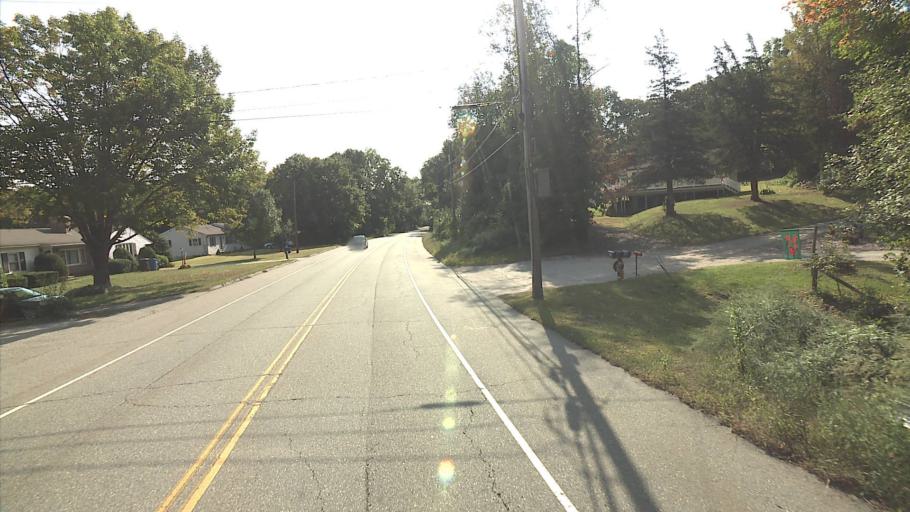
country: US
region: Connecticut
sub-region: New London County
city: Baltic
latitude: 41.5831
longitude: -72.1491
